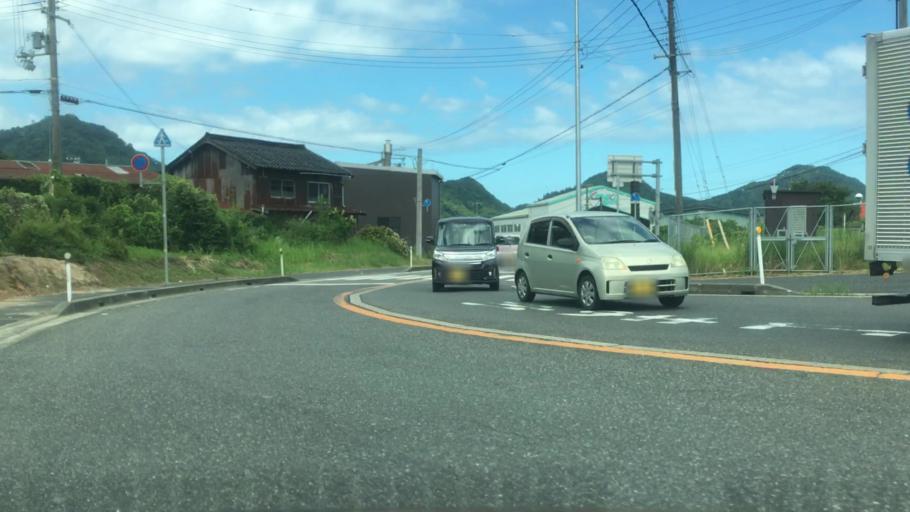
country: JP
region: Tottori
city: Tottori
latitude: 35.6190
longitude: 134.4617
